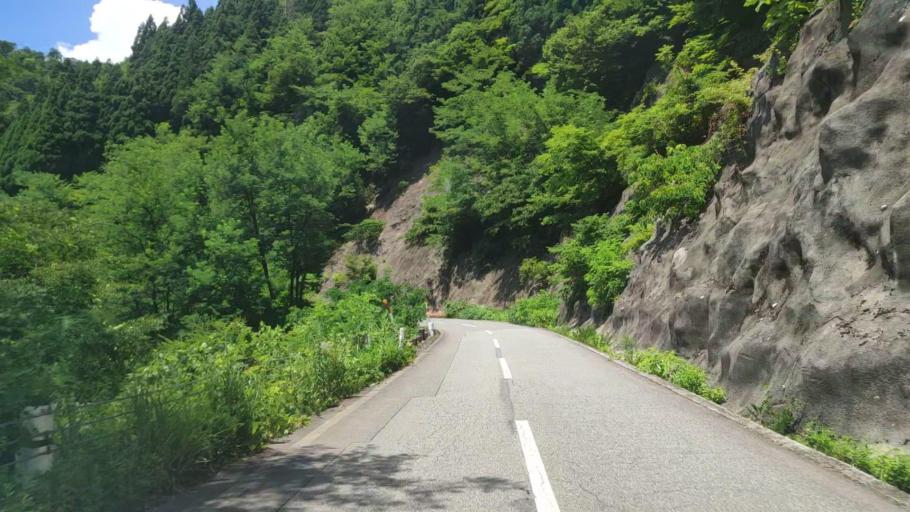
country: JP
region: Fukui
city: Ono
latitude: 35.9016
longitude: 136.5164
